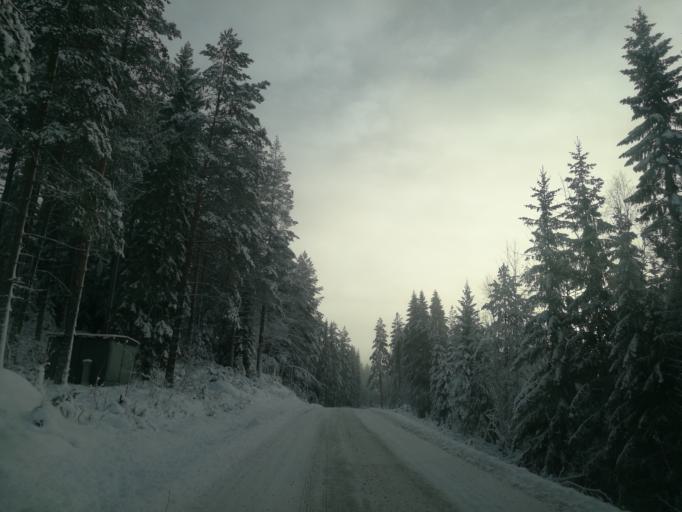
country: SE
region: Vaermland
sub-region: Torsby Kommun
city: Torsby
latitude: 60.6461
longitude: 12.7299
